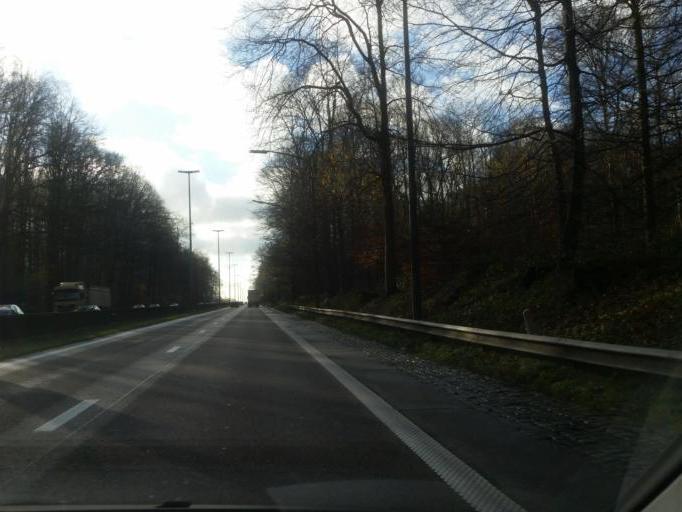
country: BE
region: Flanders
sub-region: Provincie Vlaams-Brabant
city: Hoeilaart
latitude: 50.7950
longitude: 4.4609
